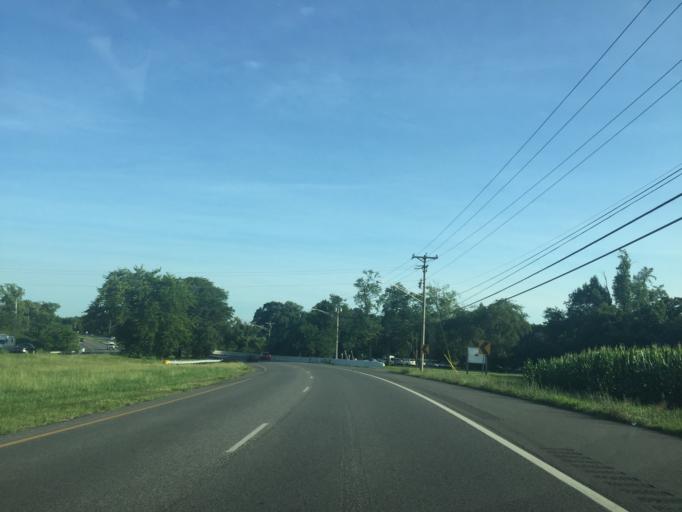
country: US
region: Delaware
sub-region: Kent County
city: Cheswold
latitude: 39.2458
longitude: -75.5884
